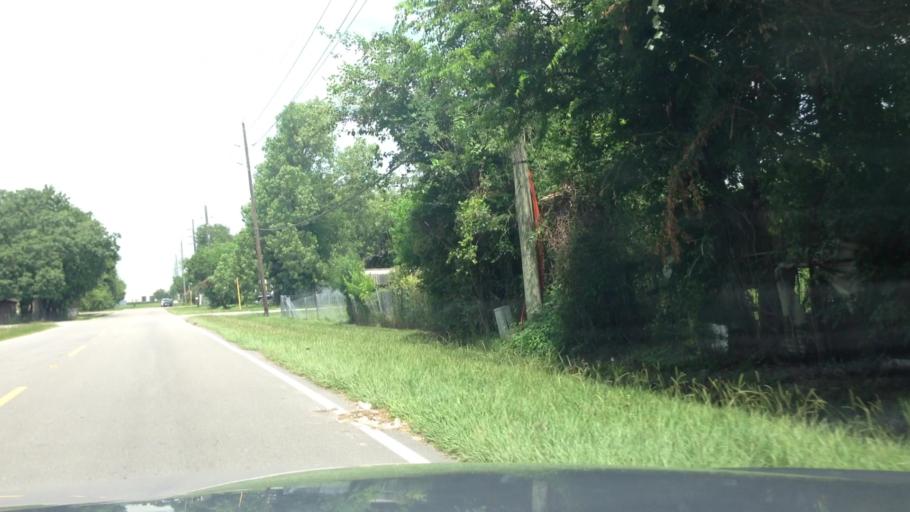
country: US
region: Texas
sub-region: Harris County
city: Jersey Village
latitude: 29.9104
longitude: -95.5479
